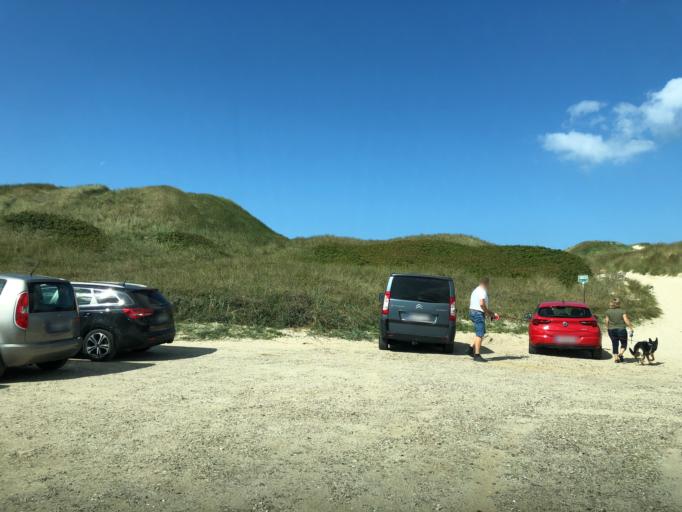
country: DK
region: Central Jutland
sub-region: Ringkobing-Skjern Kommune
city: Ringkobing
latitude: 56.1760
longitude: 8.1238
